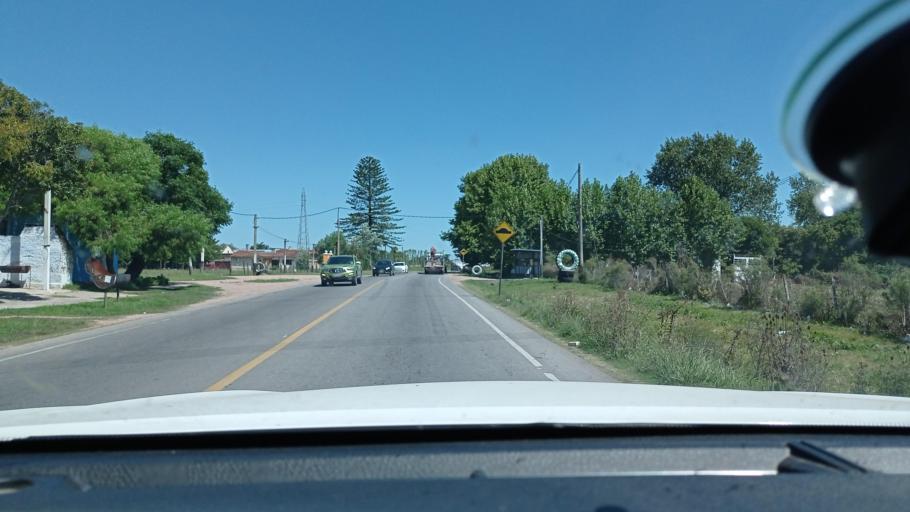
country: UY
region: Canelones
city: La Paz
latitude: -34.7787
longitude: -56.1672
